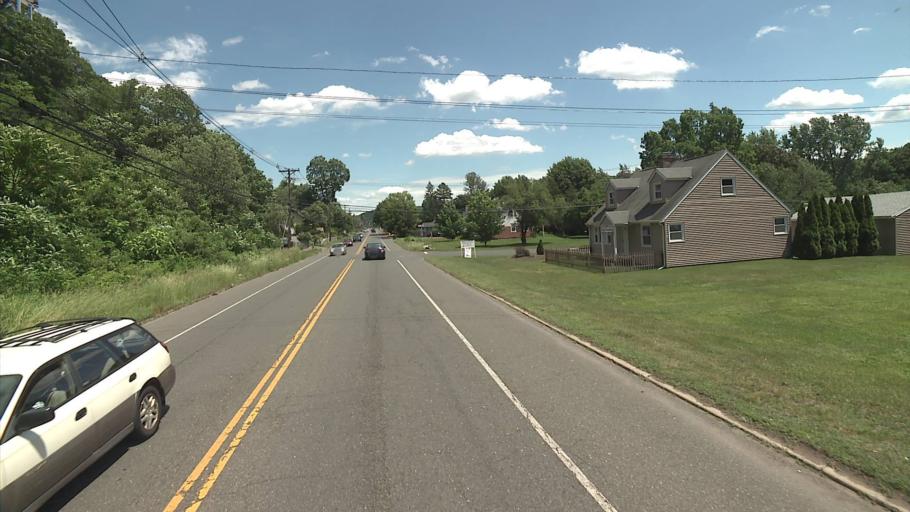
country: US
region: Connecticut
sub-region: New Haven County
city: Naugatuck
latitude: 41.4705
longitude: -73.0357
